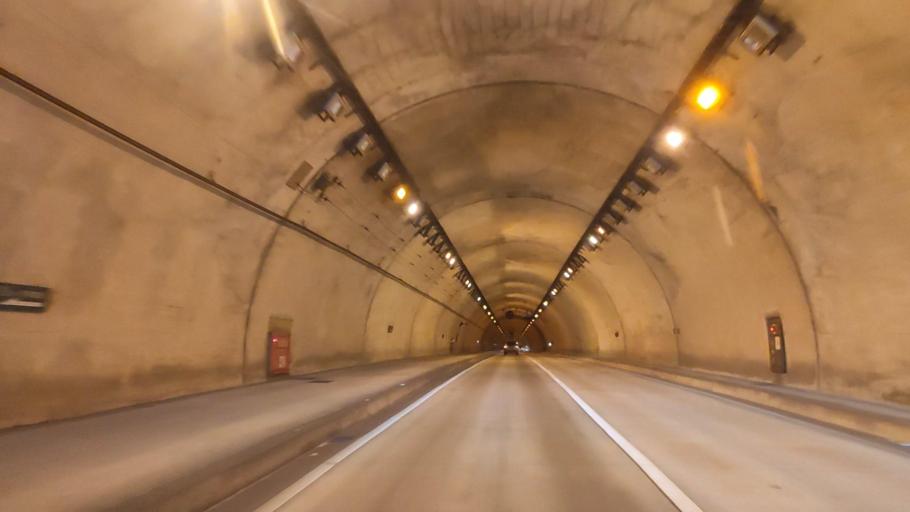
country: JP
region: Ehime
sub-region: Shikoku-chuo Shi
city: Matsuyama
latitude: 33.8762
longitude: 132.7142
